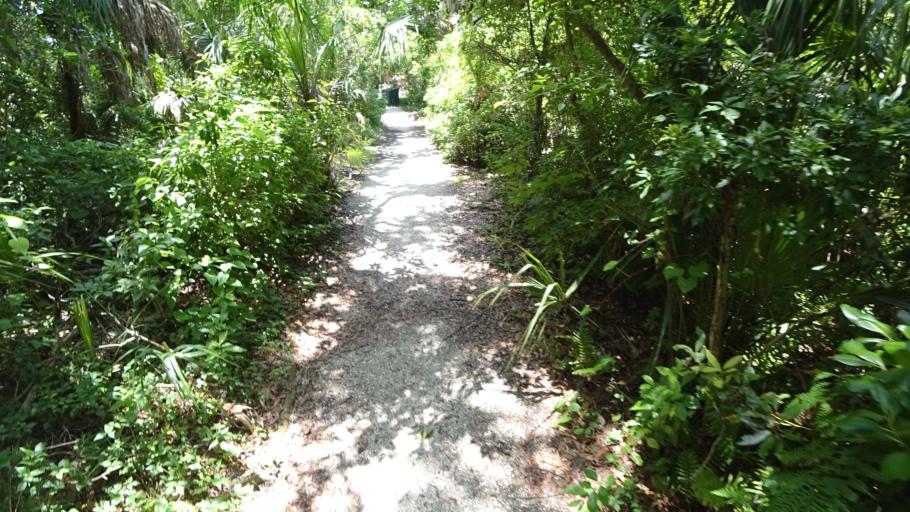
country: US
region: Florida
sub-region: Manatee County
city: West Bradenton
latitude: 27.5212
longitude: -82.6443
